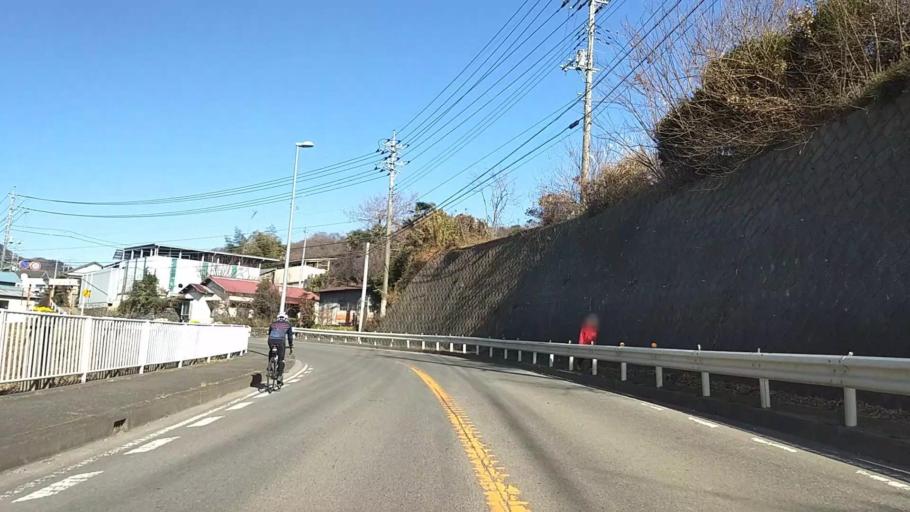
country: JP
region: Kanagawa
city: Atsugi
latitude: 35.4732
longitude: 139.3113
